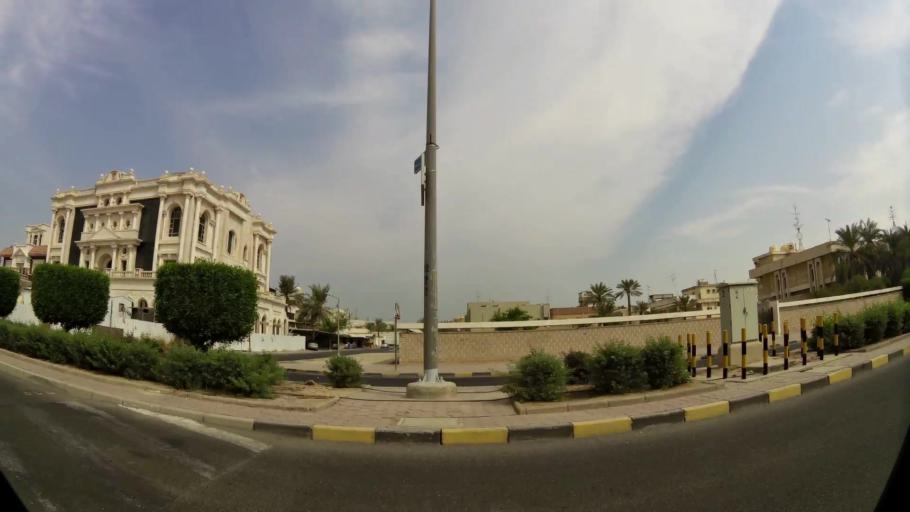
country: KW
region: Al Asimah
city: Kuwait City
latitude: 29.3516
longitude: 47.9859
